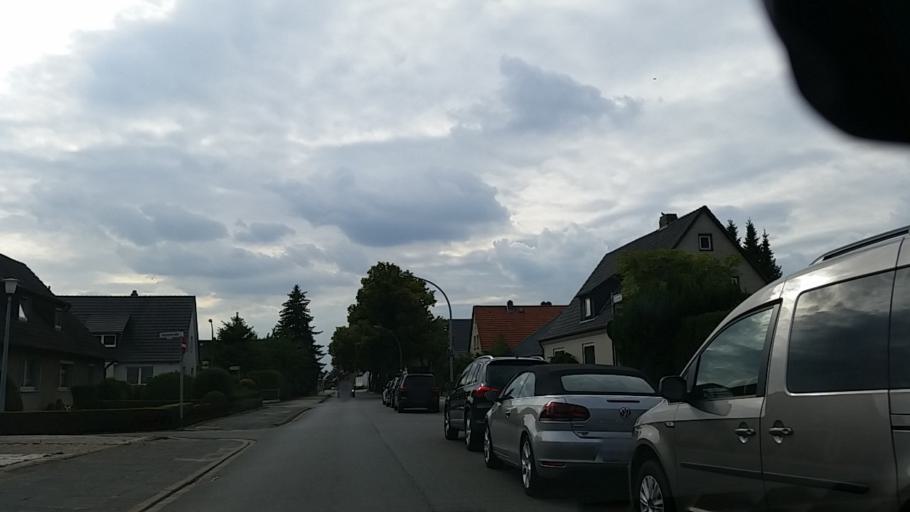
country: DE
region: Lower Saxony
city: Weyhausen
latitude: 52.4210
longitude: 10.7077
